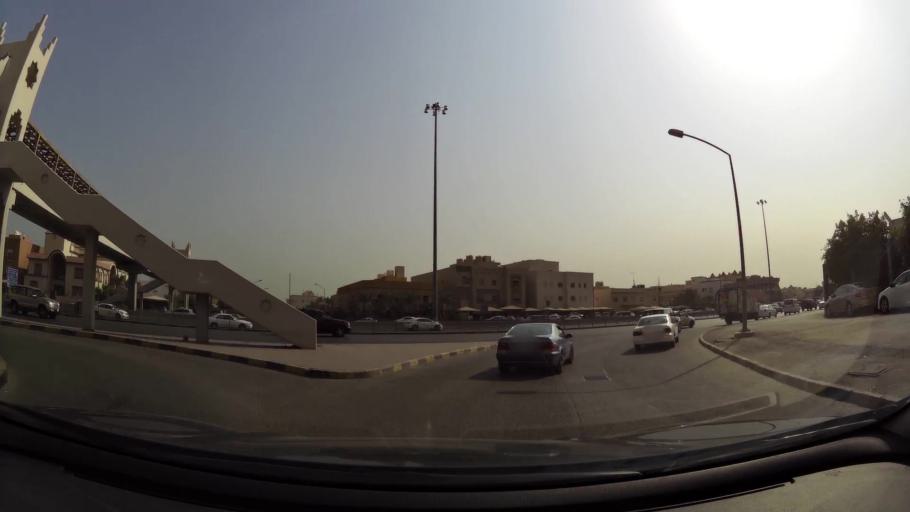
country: KW
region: Muhafazat Hawalli
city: Ar Rumaythiyah
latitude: 29.3211
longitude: 48.0612
